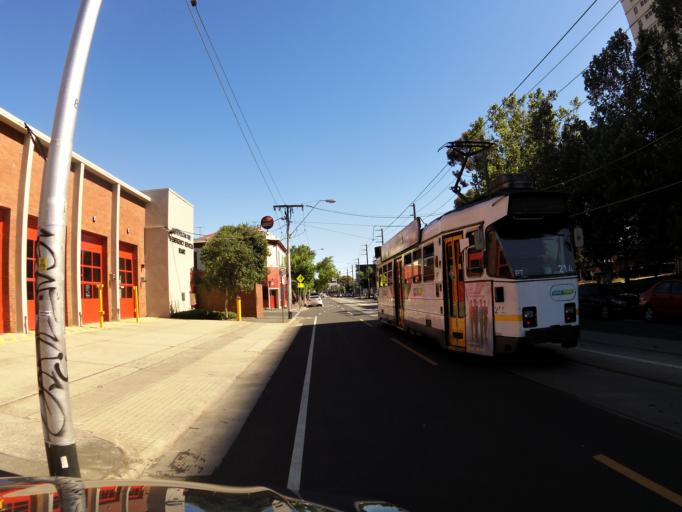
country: AU
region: Victoria
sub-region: Yarra
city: Richmond
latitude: -37.8123
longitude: 145.0004
